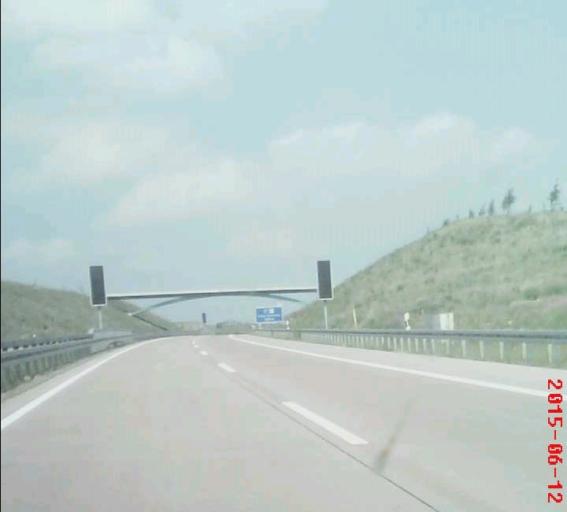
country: DE
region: Thuringia
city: Bretleben
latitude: 51.3197
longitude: 11.2400
